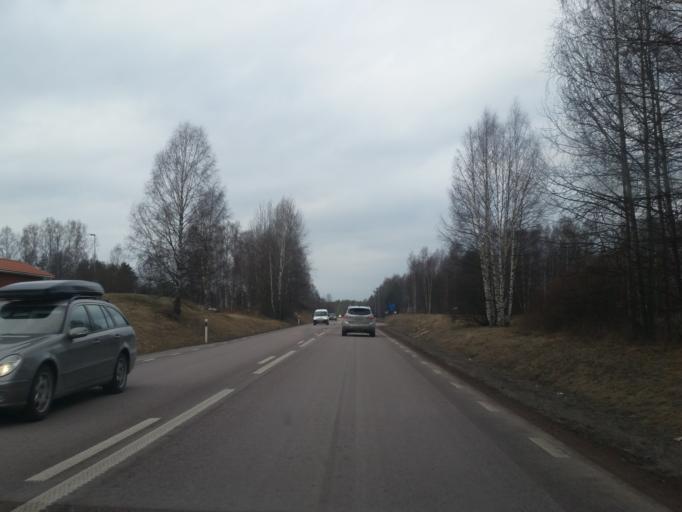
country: SE
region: Dalarna
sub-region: Mora Kommun
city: Mora
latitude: 61.0299
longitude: 14.5251
